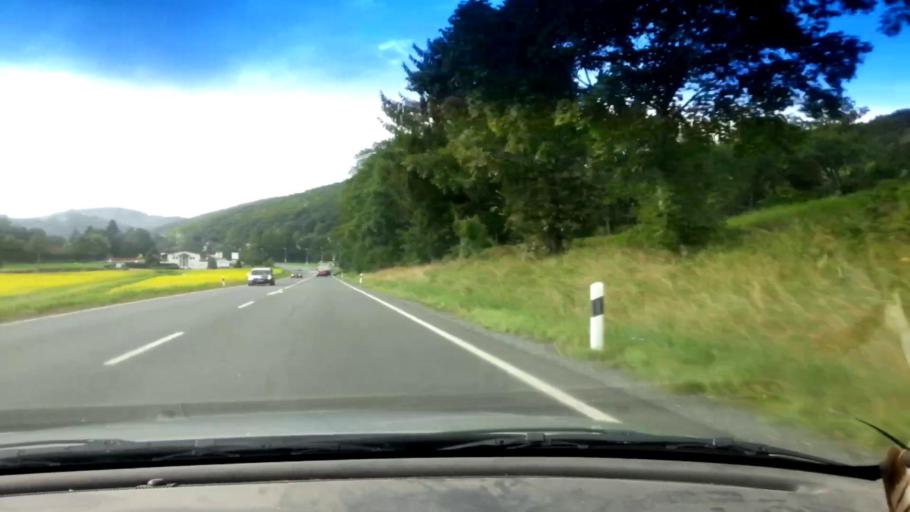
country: DE
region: Bavaria
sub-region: Upper Franconia
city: Bad Berneck im Fichtelgebirge
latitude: 50.0340
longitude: 11.6843
